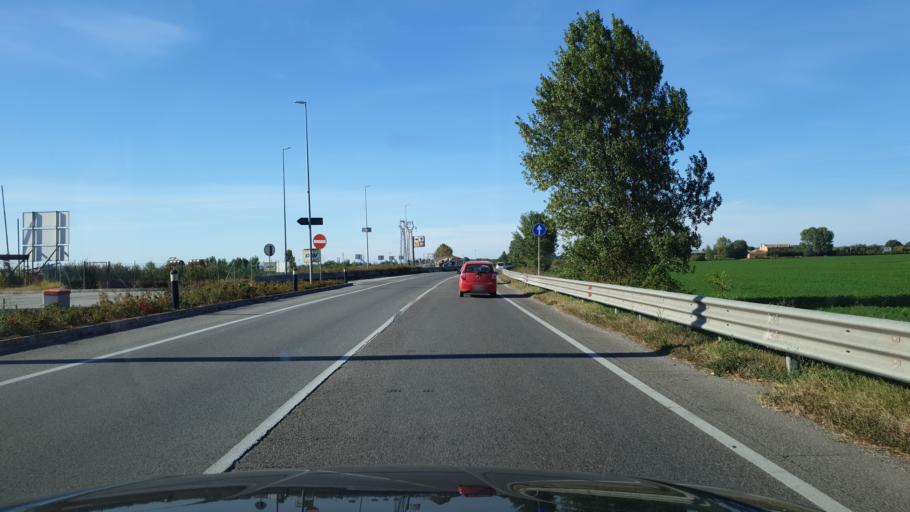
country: IT
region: Emilia-Romagna
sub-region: Provincia di Ravenna
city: Savio
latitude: 44.3097
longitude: 12.2854
